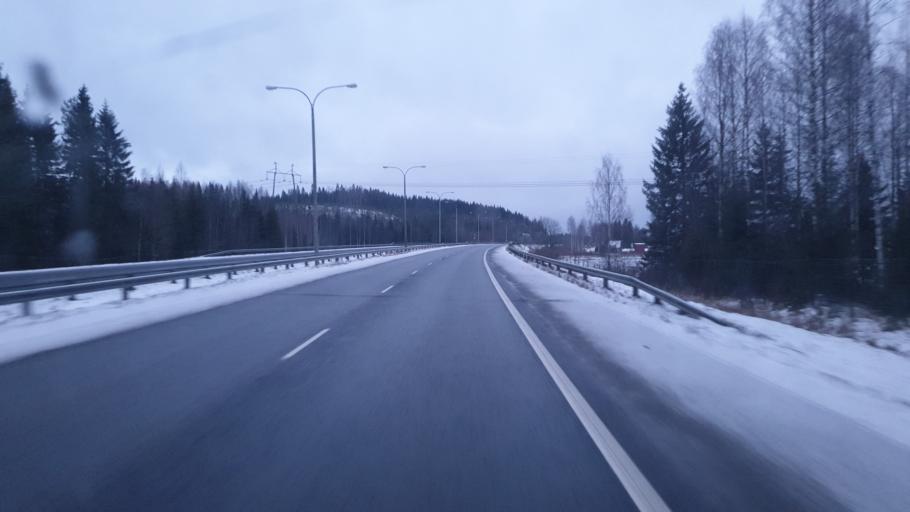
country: FI
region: Northern Savo
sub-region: Kuopio
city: Siilinjaervi
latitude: 63.0434
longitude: 27.6625
